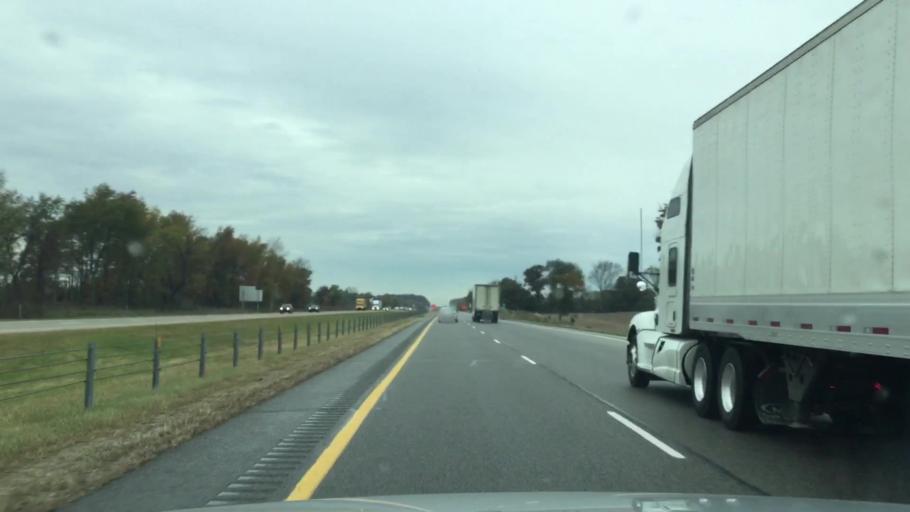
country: US
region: Michigan
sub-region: Calhoun County
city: Albion
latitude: 42.2838
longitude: -84.8057
